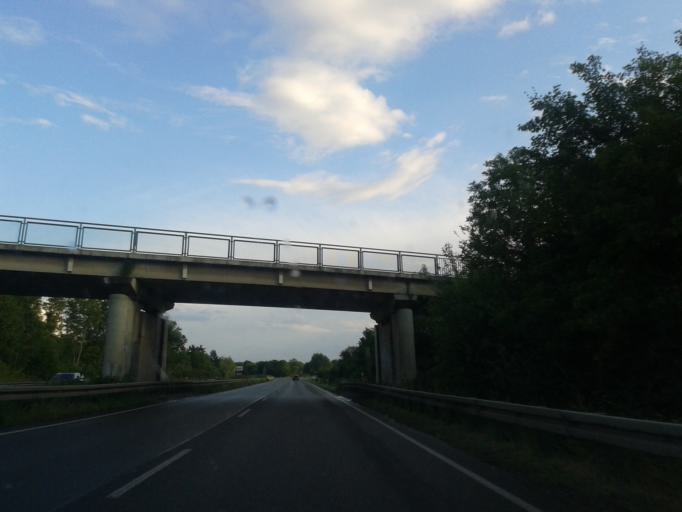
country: DE
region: Saxony
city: Markkleeberg
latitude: 51.2733
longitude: 12.3824
